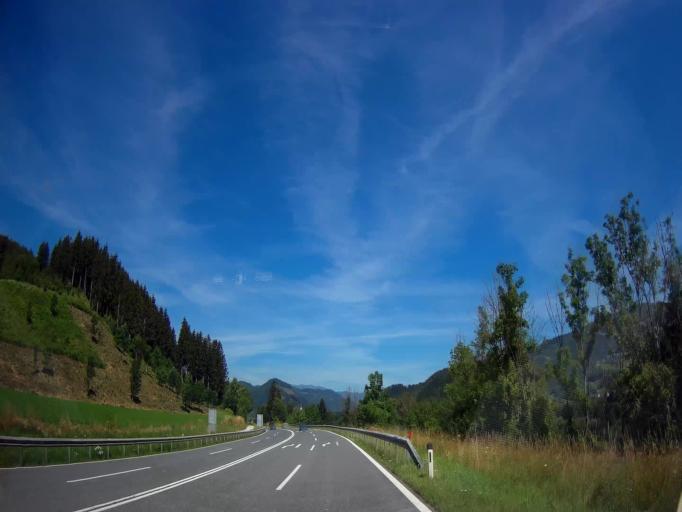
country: AT
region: Carinthia
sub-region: Politischer Bezirk Sankt Veit an der Glan
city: Althofen
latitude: 46.8788
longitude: 14.4505
